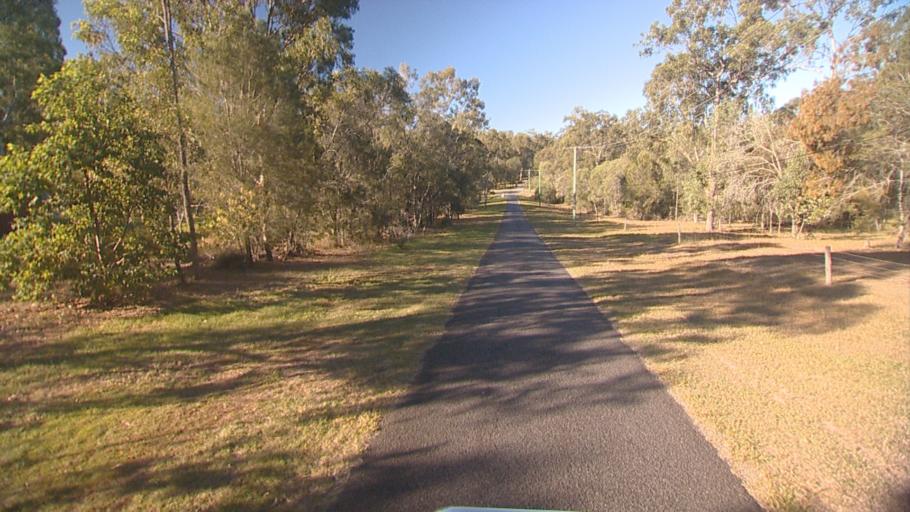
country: AU
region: Queensland
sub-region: Logan
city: Park Ridge South
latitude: -27.7408
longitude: 153.0188
